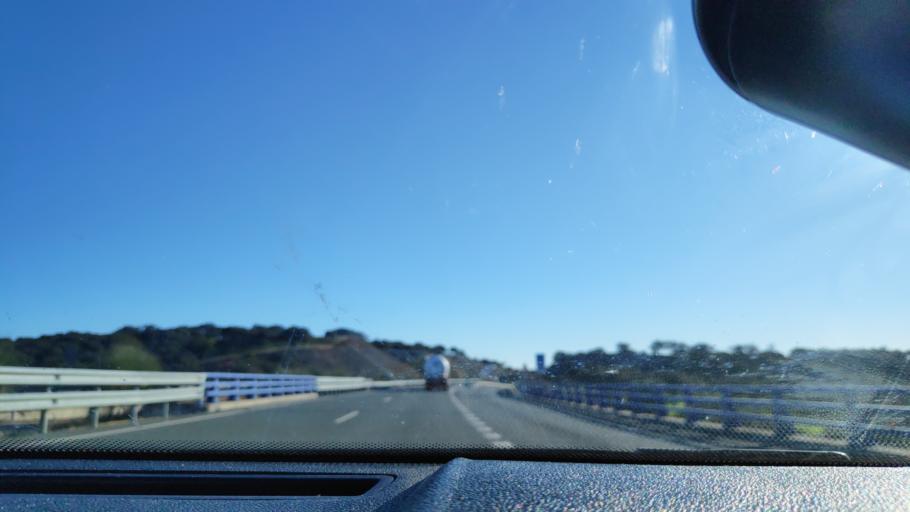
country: ES
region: Andalusia
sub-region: Provincia de Huelva
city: Santa Olalla del Cala
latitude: 37.9056
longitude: -6.2136
